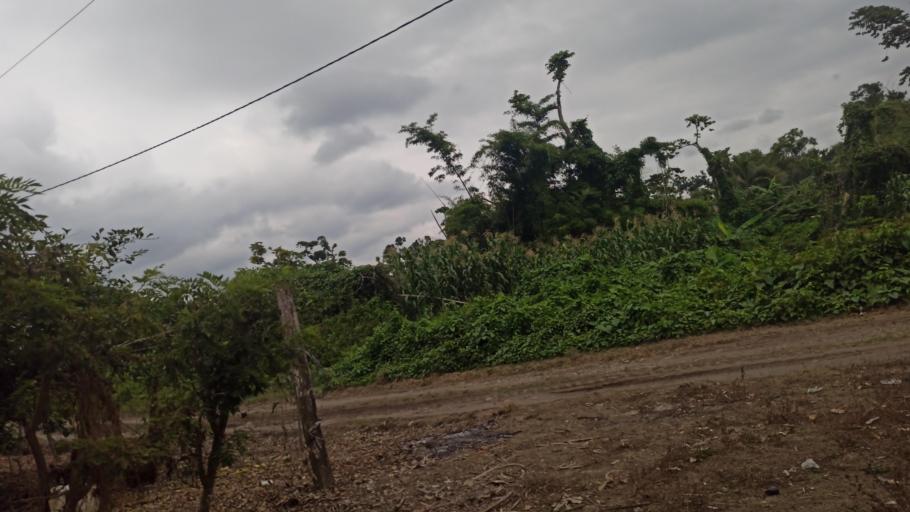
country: MX
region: Veracruz
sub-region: Papantla
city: El Chote
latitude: 20.3647
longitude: -97.4313
